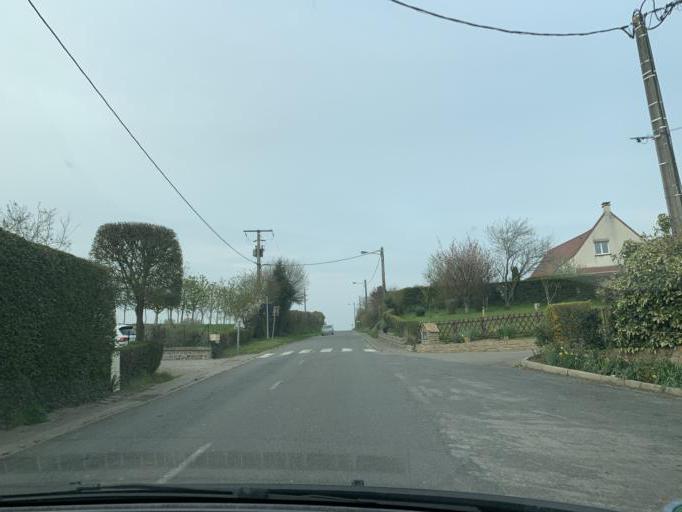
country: FR
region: Nord-Pas-de-Calais
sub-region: Departement du Pas-de-Calais
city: Samer
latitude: 50.6855
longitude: 1.7618
